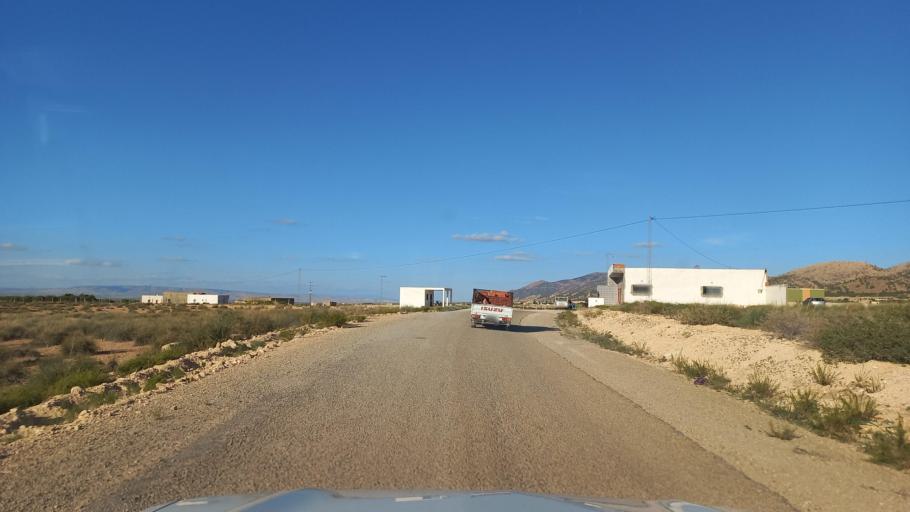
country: TN
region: Al Qasrayn
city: Sbiba
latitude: 35.3558
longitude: 9.1376
